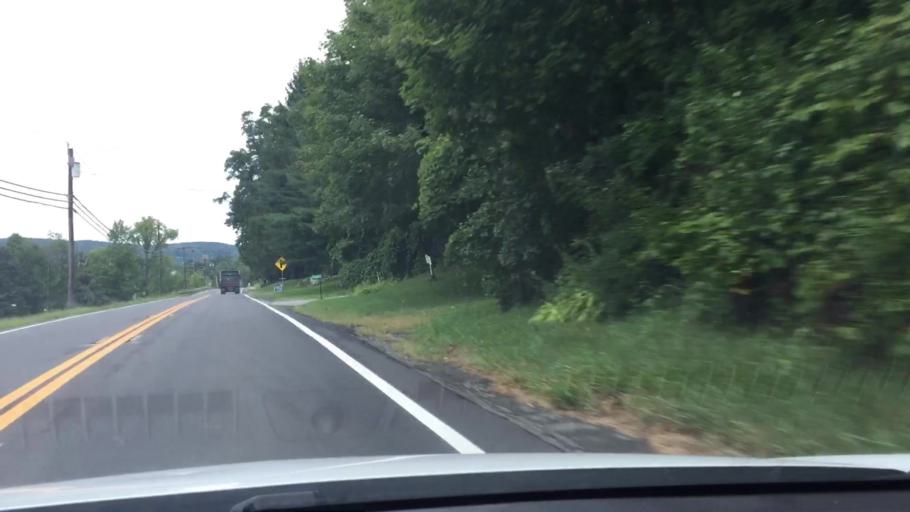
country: US
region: Massachusetts
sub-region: Berkshire County
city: Richmond
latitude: 42.3708
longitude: -73.3680
